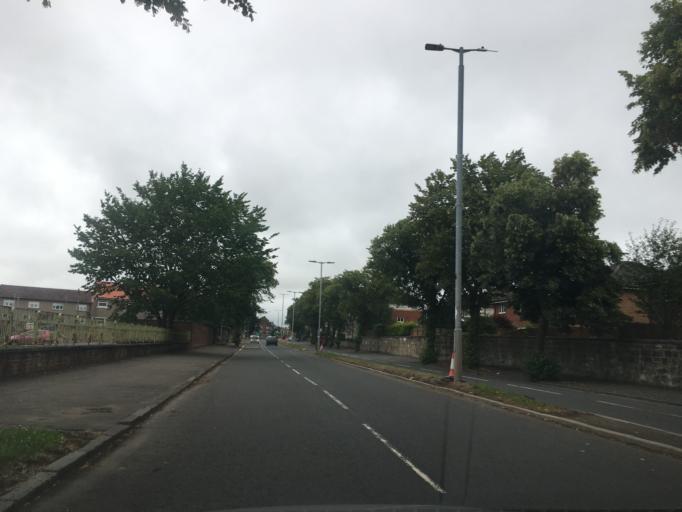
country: GB
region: Scotland
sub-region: Renfrewshire
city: Renfrew
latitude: 55.8750
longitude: -4.3796
